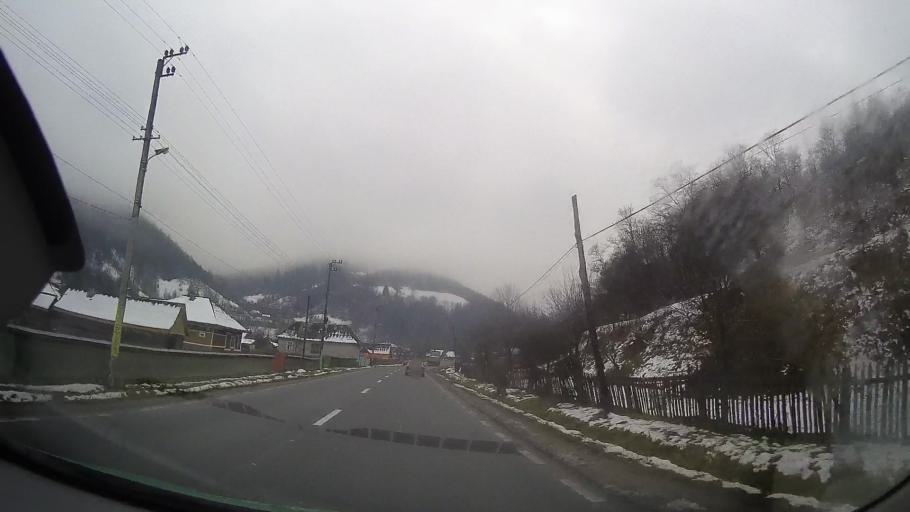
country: RO
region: Neamt
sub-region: Comuna Bicazu Ardelean
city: Bicazu Ardelean
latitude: 46.8561
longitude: 25.9359
